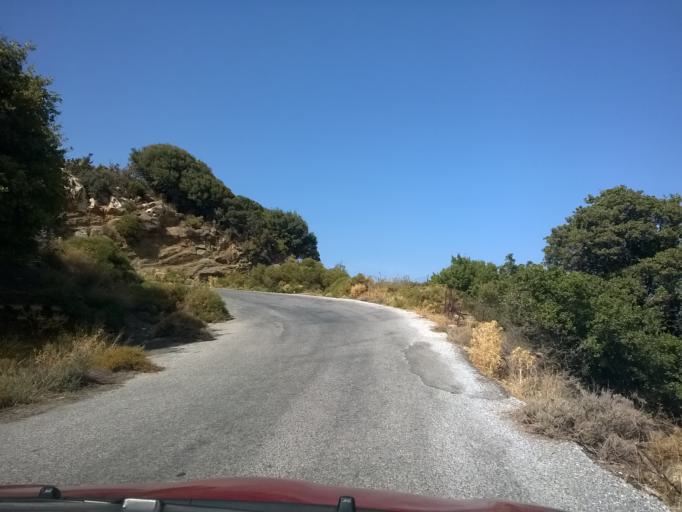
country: GR
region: South Aegean
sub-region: Nomos Kykladon
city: Filotion
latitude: 37.0264
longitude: 25.4824
